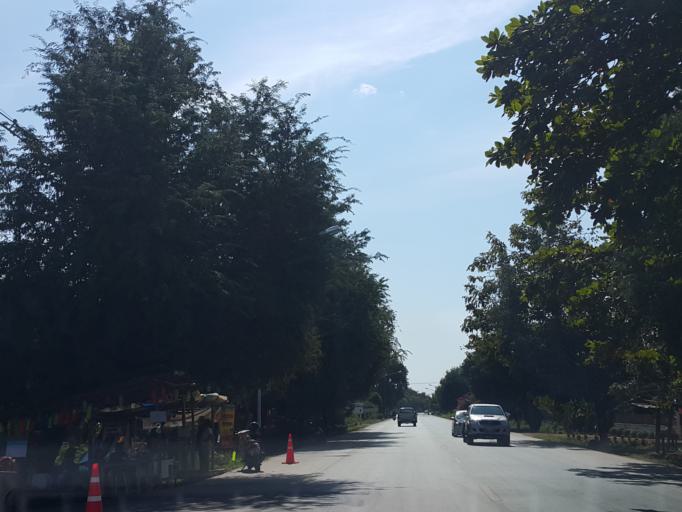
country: TH
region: Sukhothai
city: Sawankhalok
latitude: 17.2828
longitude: 99.8442
